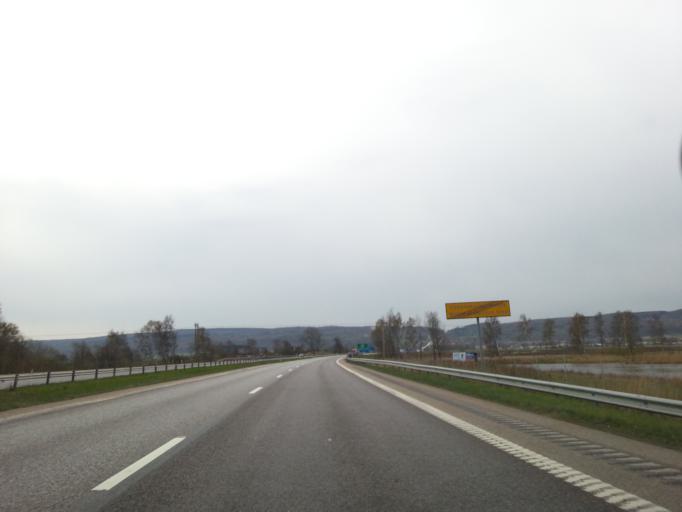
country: SE
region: Halland
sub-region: Laholms Kommun
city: Mellbystrand
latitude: 56.4431
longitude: 12.9541
